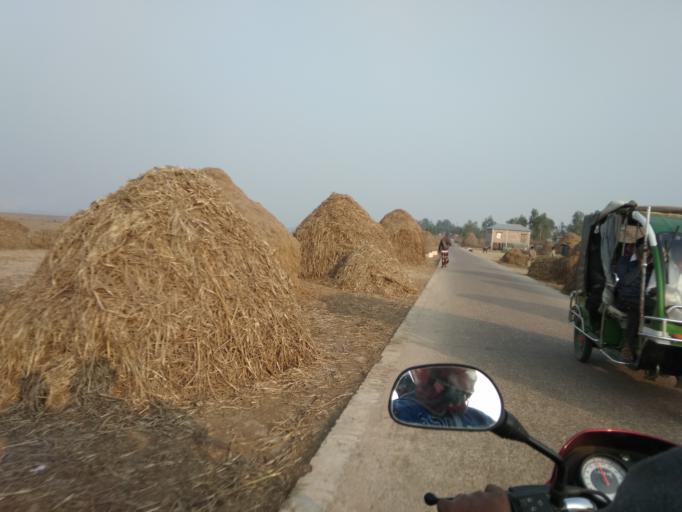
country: BD
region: Rajshahi
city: Ishurdi
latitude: 24.4812
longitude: 89.2312
